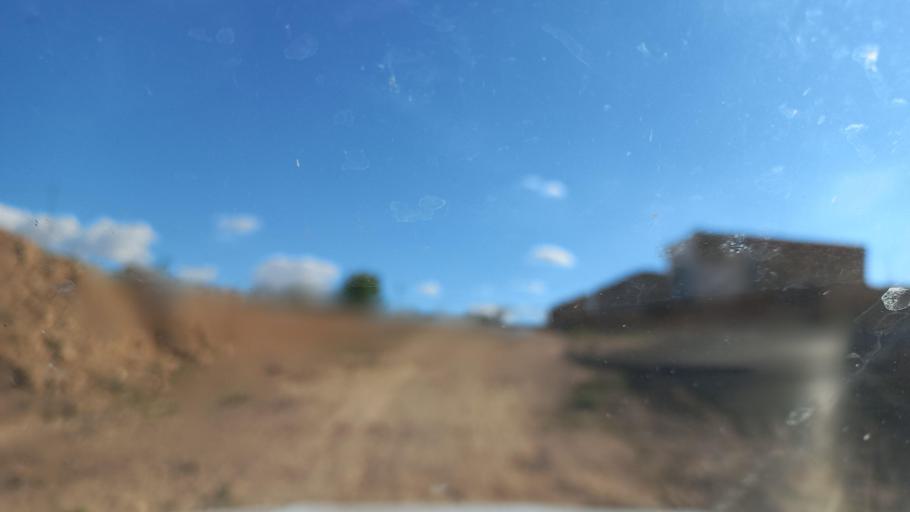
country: TN
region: Al Qasrayn
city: Sbiba
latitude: 35.3858
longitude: 9.0240
